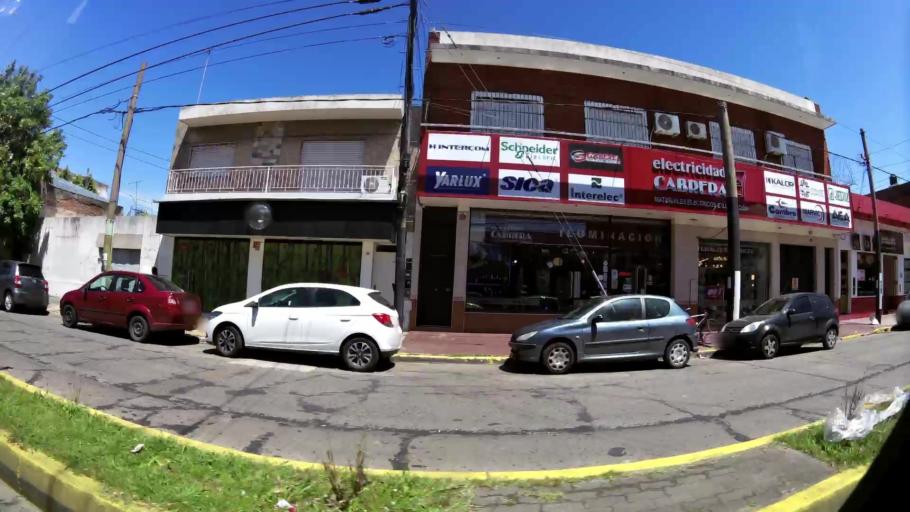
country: AR
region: Buenos Aires
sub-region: Partido de Quilmes
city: Quilmes
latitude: -34.7284
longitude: -58.2670
